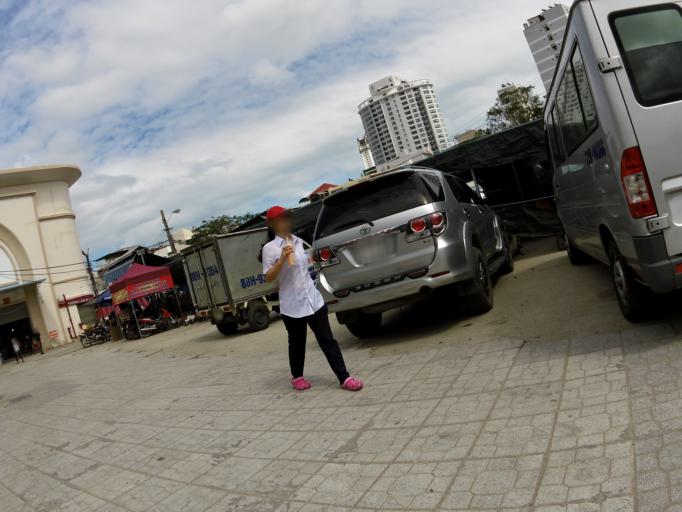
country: VN
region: Khanh Hoa
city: Nha Trang
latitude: 12.2548
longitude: 109.1922
